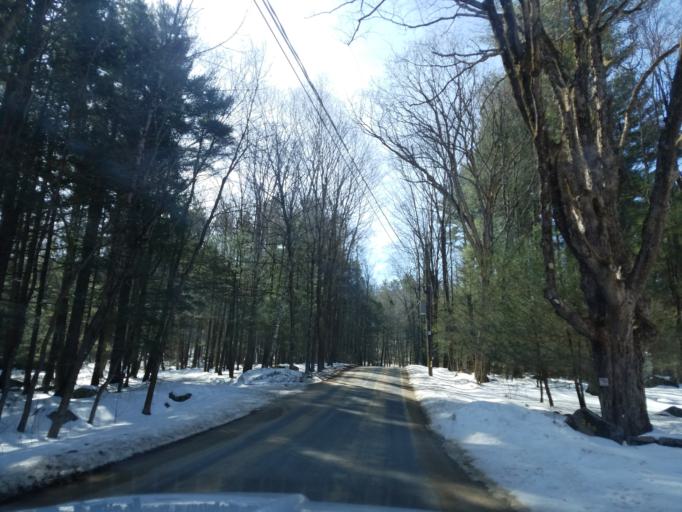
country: US
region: Connecticut
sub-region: Litchfield County
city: Canaan
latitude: 41.8732
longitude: -73.3521
